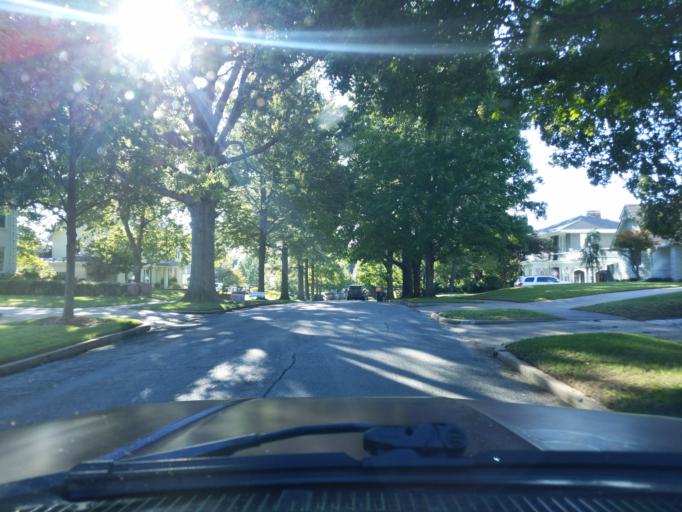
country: US
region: Oklahoma
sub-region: Tulsa County
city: Tulsa
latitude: 36.1342
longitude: -95.9792
